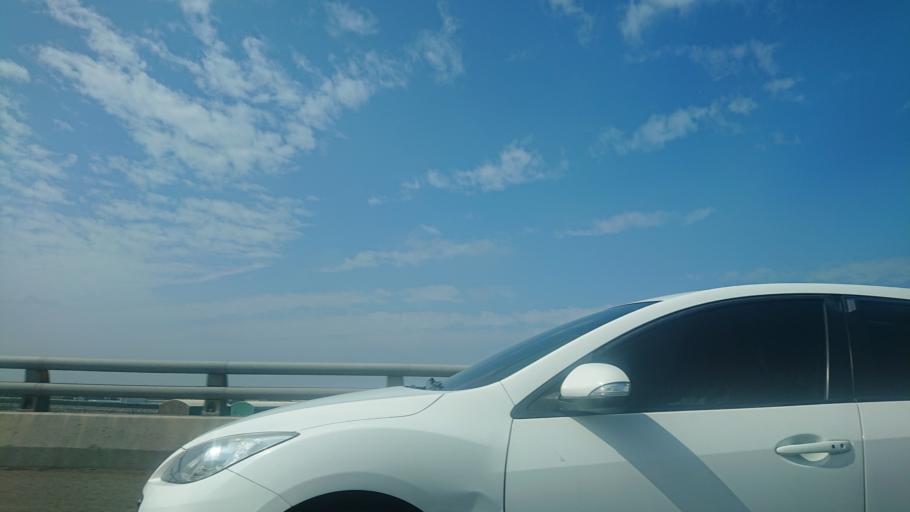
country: TW
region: Taiwan
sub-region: Changhua
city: Chang-hua
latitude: 24.0494
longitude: 120.4059
